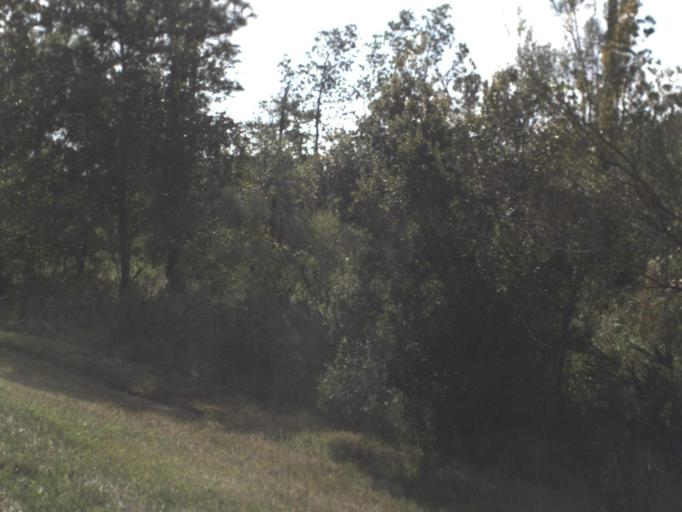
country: US
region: Florida
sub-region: Osceola County
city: Poinciana
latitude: 28.1764
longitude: -81.4518
